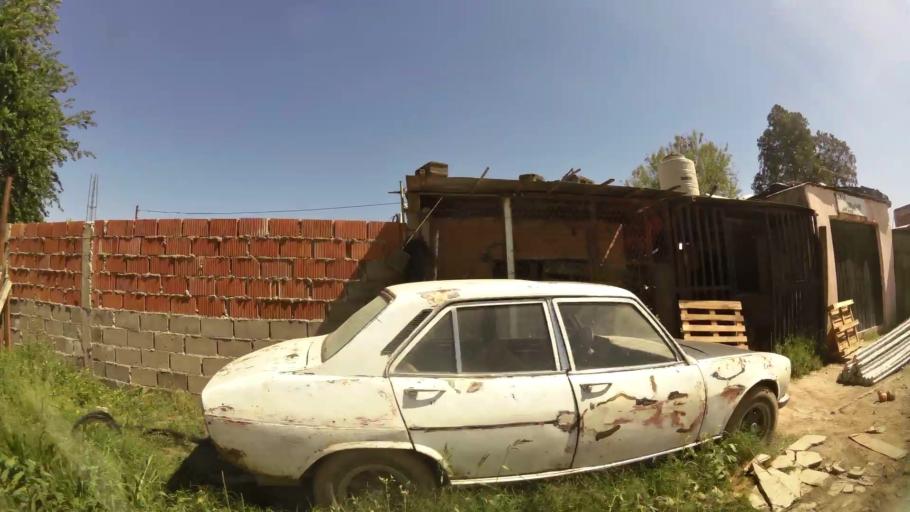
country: AR
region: Cordoba
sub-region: Departamento de Capital
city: Cordoba
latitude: -31.3638
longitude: -64.1418
